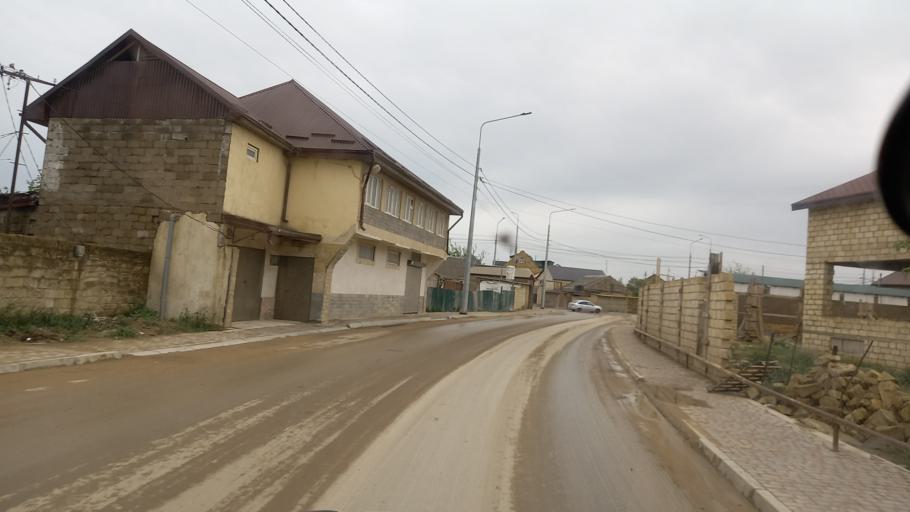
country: RU
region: Dagestan
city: Derbent
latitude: 42.1015
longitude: 48.2816
